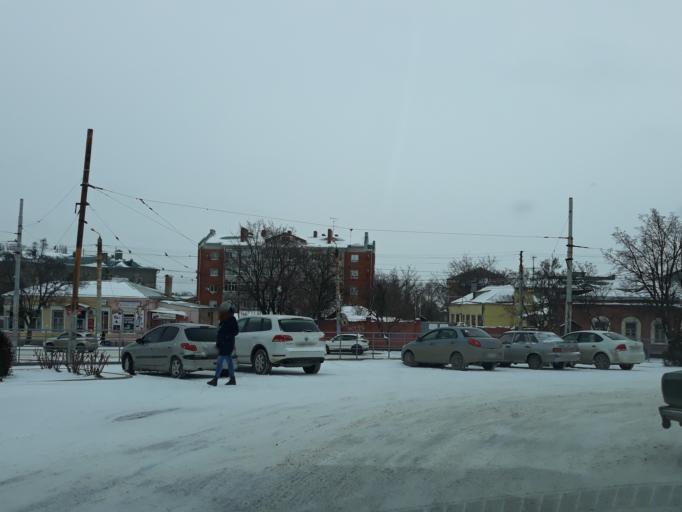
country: RU
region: Rostov
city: Taganrog
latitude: 47.2203
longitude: 38.9168
